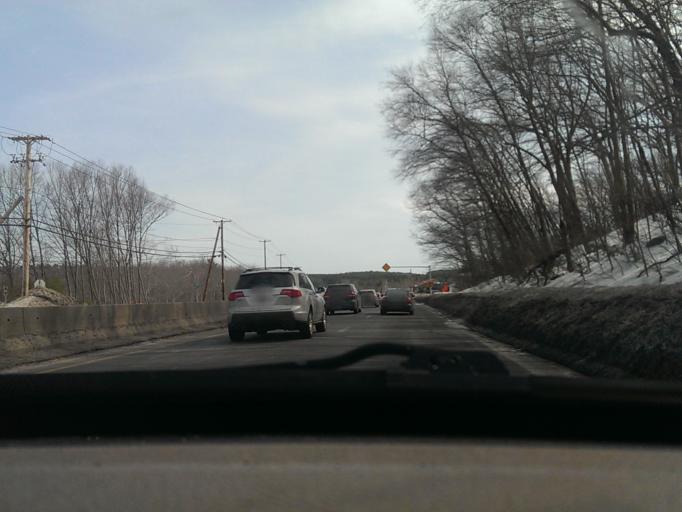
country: US
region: Massachusetts
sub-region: Worcester County
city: Sutton
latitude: 42.1636
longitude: -71.7425
